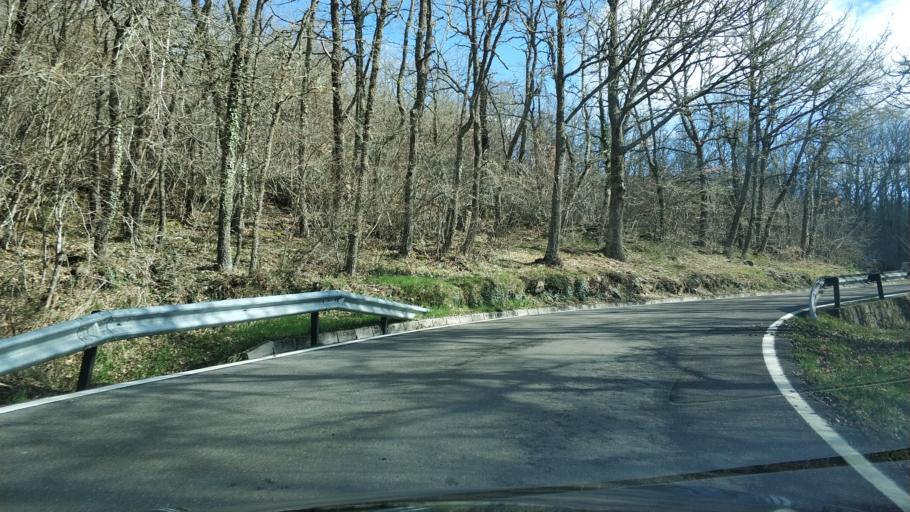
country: ES
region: Cantabria
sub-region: Provincia de Cantabria
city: Mataporquera
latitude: 42.9032
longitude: -4.0522
